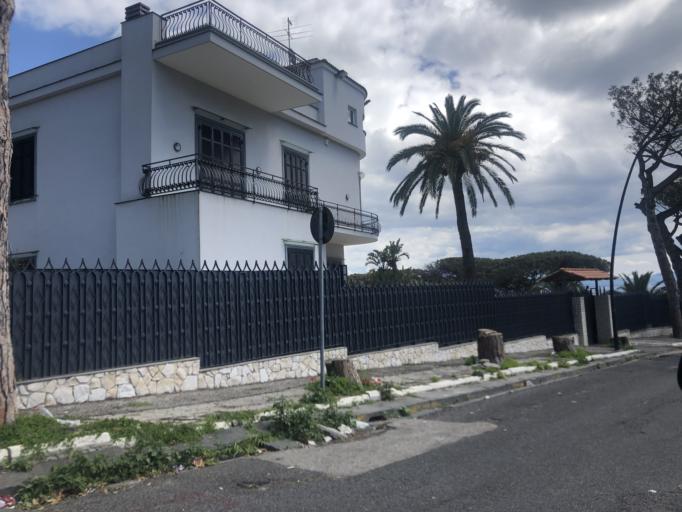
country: IT
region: Campania
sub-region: Provincia di Napoli
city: Bagnoli
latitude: 40.8000
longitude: 14.1851
